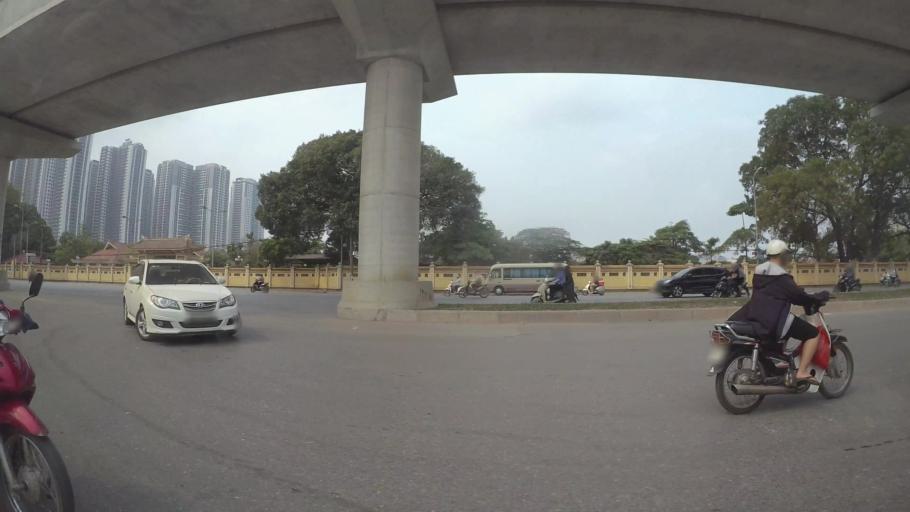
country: VN
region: Ha Noi
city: Cau Dien
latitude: 21.0388
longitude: 105.7699
